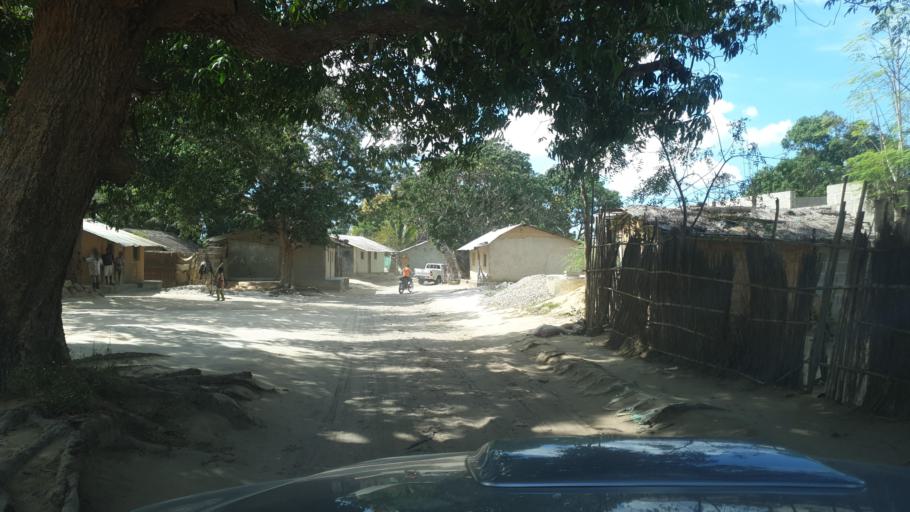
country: MZ
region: Nampula
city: Nacala
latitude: -14.5730
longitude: 40.6987
